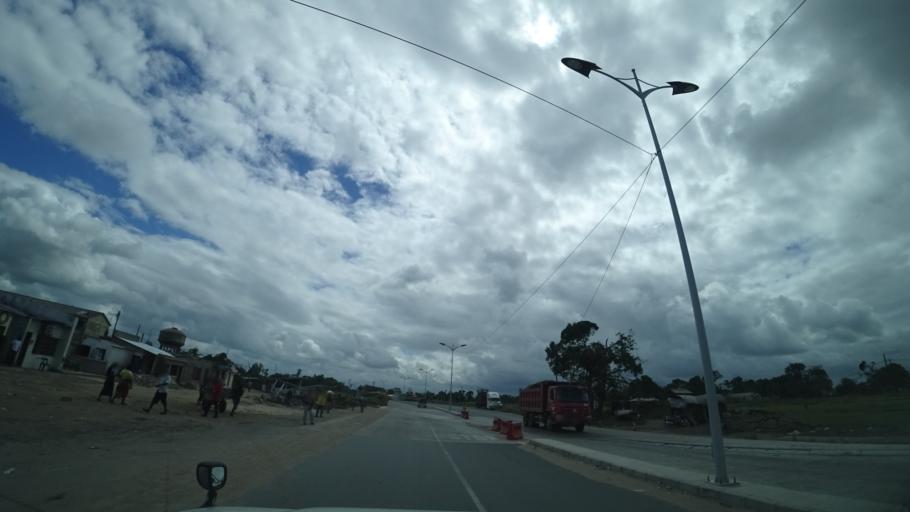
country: MZ
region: Sofala
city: Dondo
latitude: -19.6126
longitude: 34.7452
